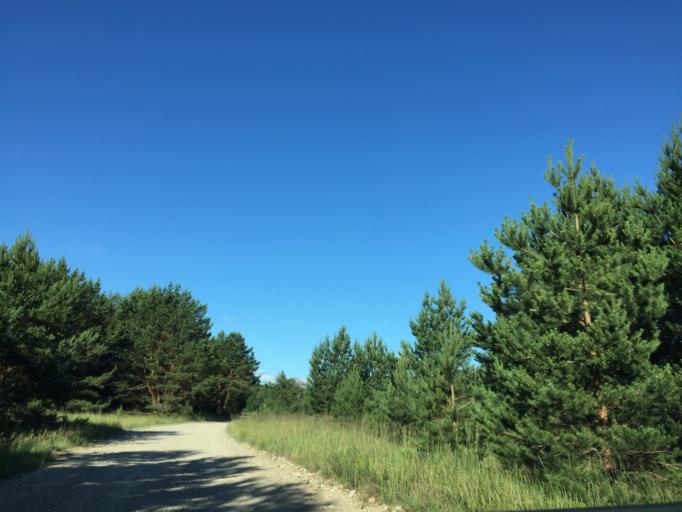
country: LV
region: Ventspils
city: Ventspils
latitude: 57.4376
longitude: 21.6090
